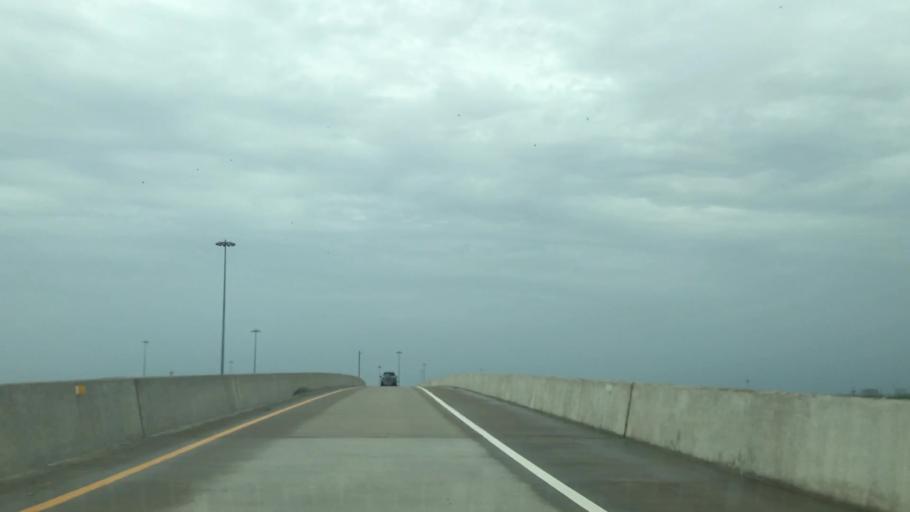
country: US
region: Texas
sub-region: Dallas County
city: Farmers Branch
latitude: 32.8644
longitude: -96.8946
